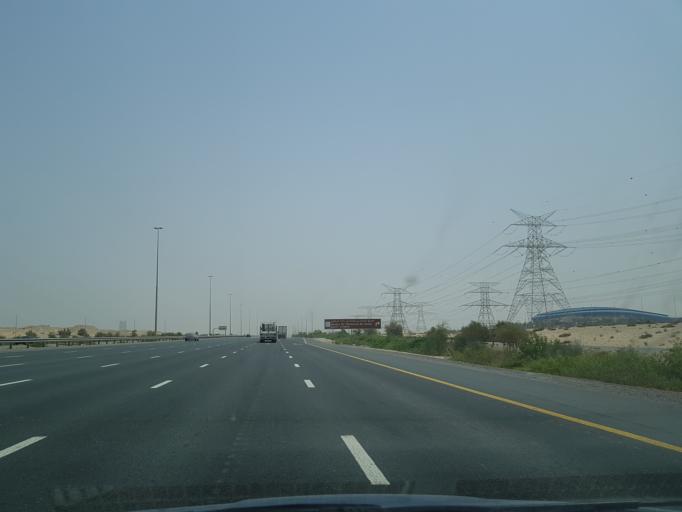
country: AE
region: Dubai
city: Dubai
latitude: 25.0483
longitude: 55.3084
